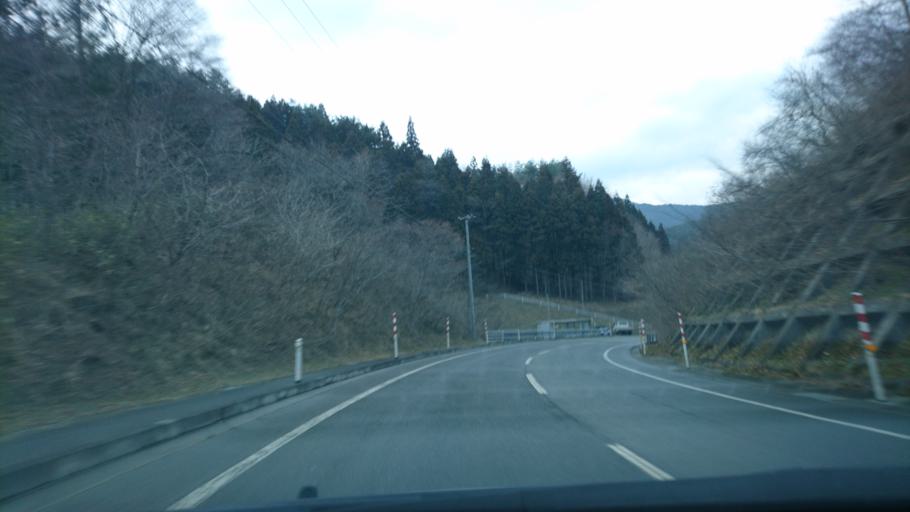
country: JP
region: Iwate
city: Ofunato
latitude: 39.0174
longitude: 141.5468
